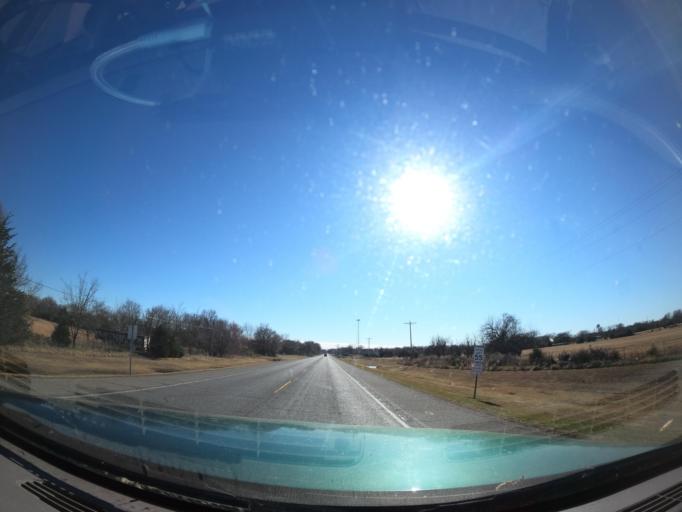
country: US
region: Oklahoma
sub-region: Muskogee County
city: Haskell
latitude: 35.8300
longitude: -95.6775
